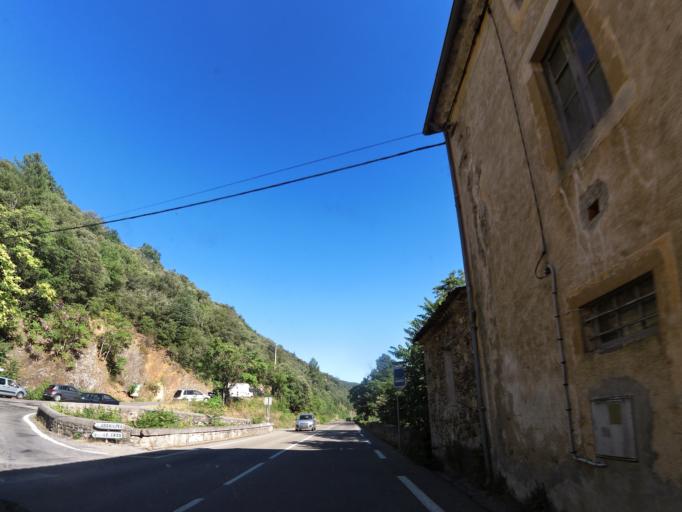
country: FR
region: Languedoc-Roussillon
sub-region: Departement du Gard
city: Valleraugue
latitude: 44.0736
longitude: 3.6713
